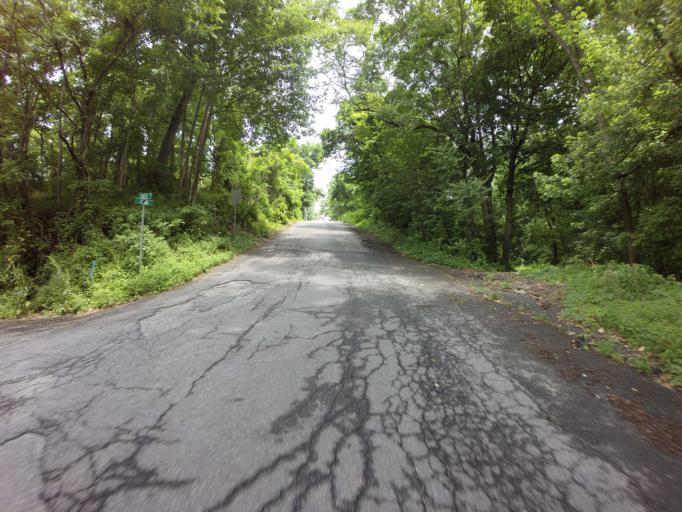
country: US
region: Maryland
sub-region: Frederick County
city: Brunswick
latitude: 39.3154
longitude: -77.6231
